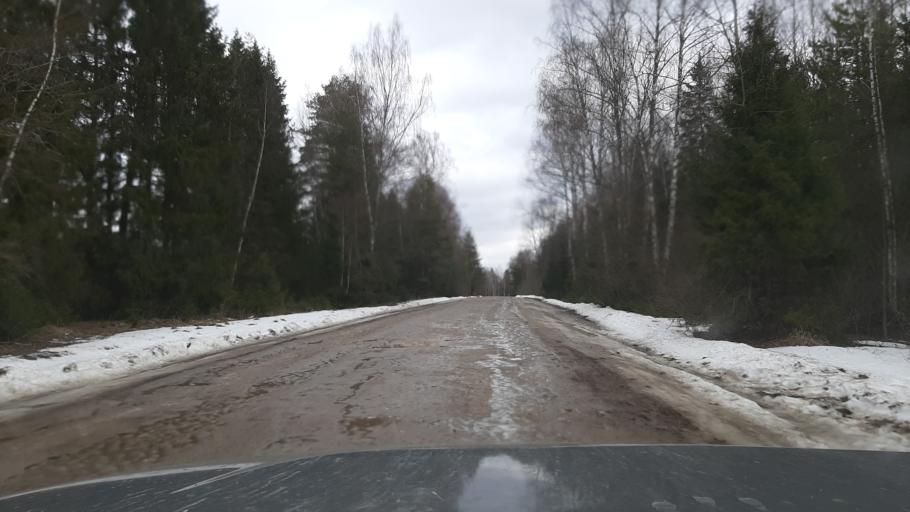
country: RU
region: Ivanovo
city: Teykovo
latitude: 56.8892
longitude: 40.6576
